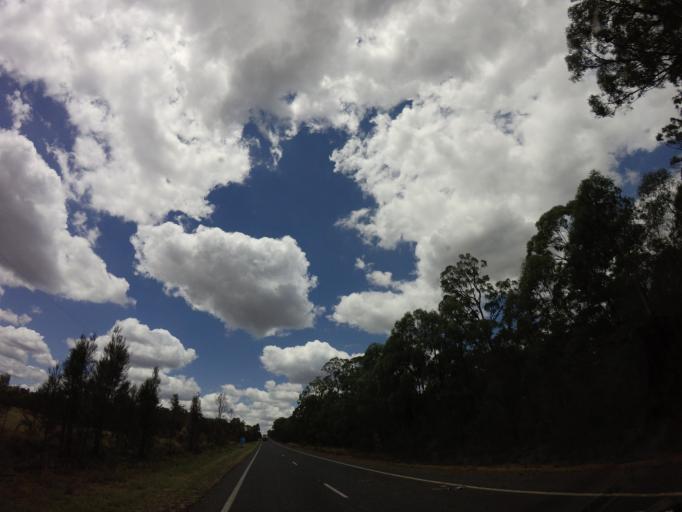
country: AU
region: Queensland
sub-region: Goondiwindi
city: Goondiwindi
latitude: -28.0032
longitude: 150.9331
